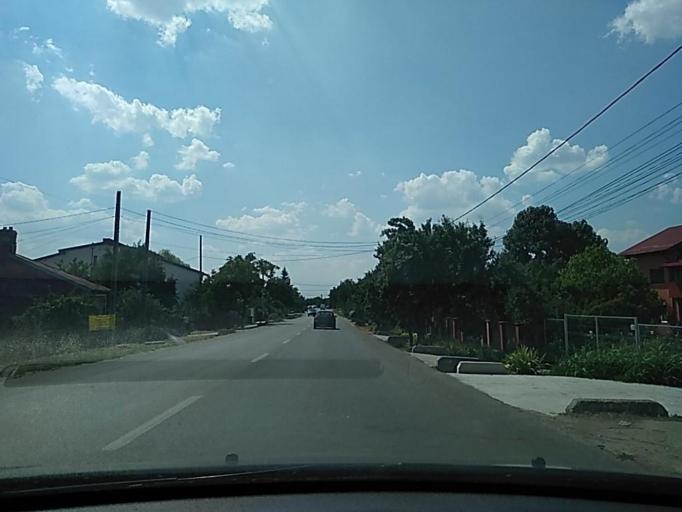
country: RO
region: Ilfov
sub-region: Comuna Clinceni
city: Olteni
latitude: 44.4032
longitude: 25.9424
